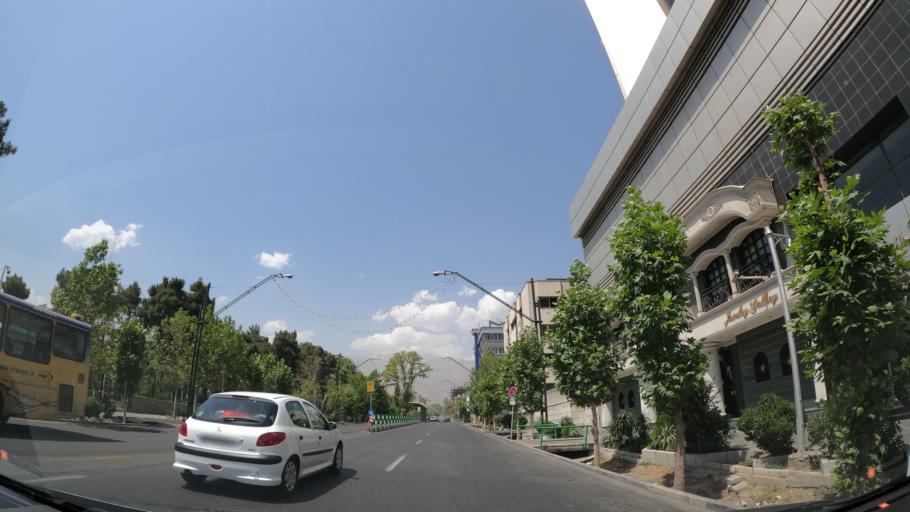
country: IR
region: Tehran
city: Tajrish
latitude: 35.7702
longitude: 51.4118
